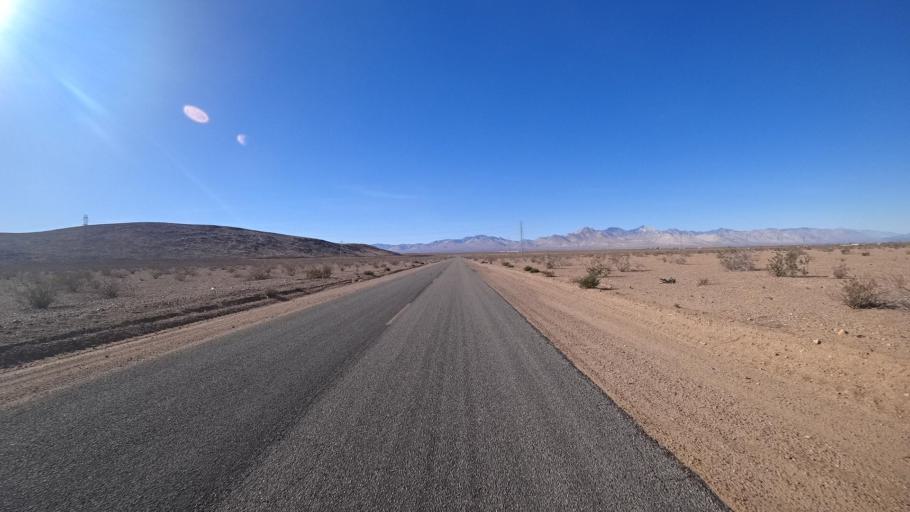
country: US
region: California
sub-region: Kern County
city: China Lake Acres
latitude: 35.5583
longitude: -117.7586
